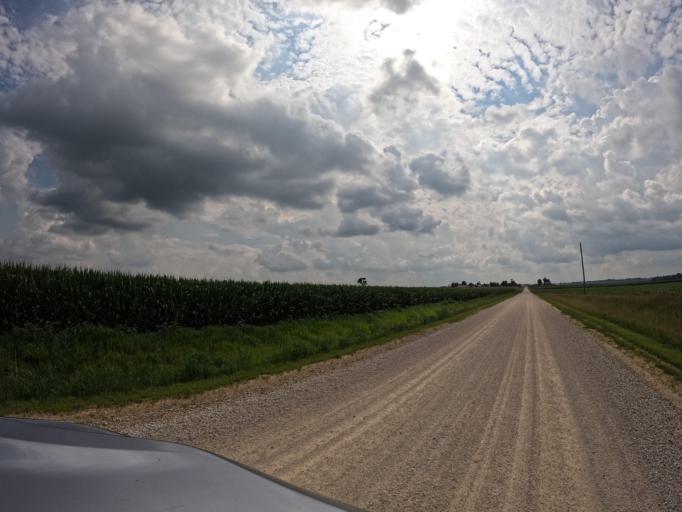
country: US
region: Iowa
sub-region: Clinton County
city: Camanche
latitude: 41.8012
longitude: -90.3894
